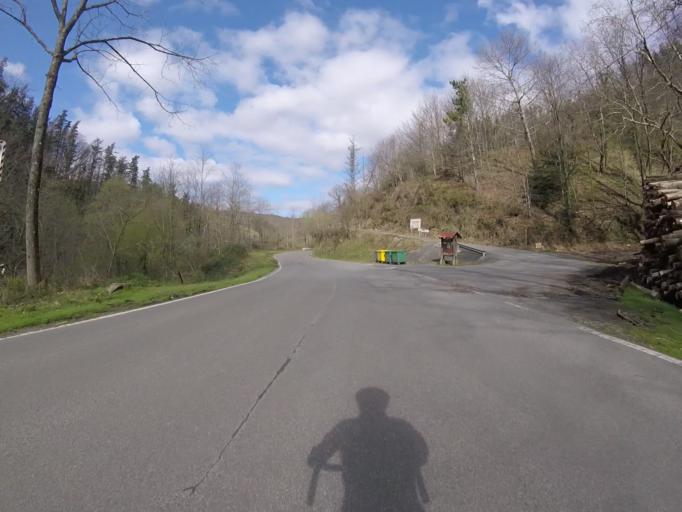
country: ES
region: Navarre
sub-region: Provincia de Navarra
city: Goizueta
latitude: 43.1646
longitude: -1.8547
